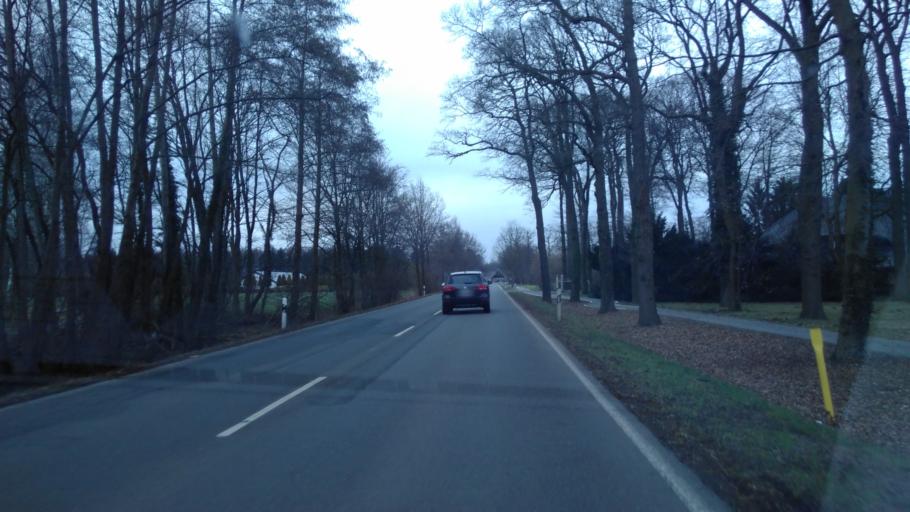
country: DE
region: North Rhine-Westphalia
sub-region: Regierungsbezirk Detmold
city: Delbruck
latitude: 51.8193
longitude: 8.5580
